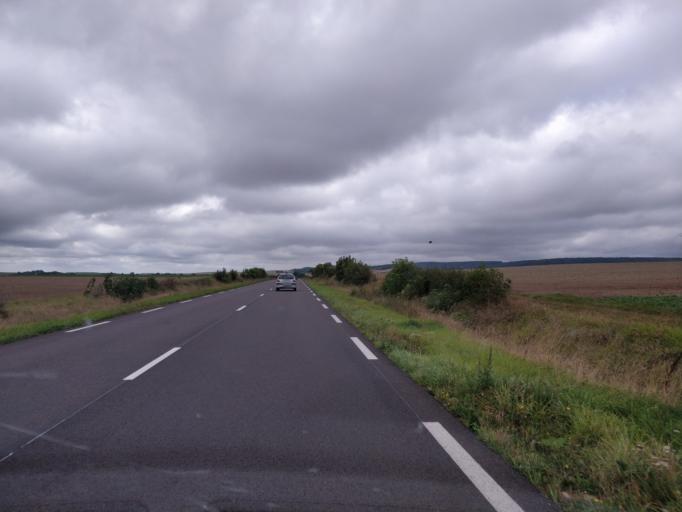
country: FR
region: Champagne-Ardenne
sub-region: Departement de l'Aube
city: Bouilly
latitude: 48.1324
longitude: 3.9809
